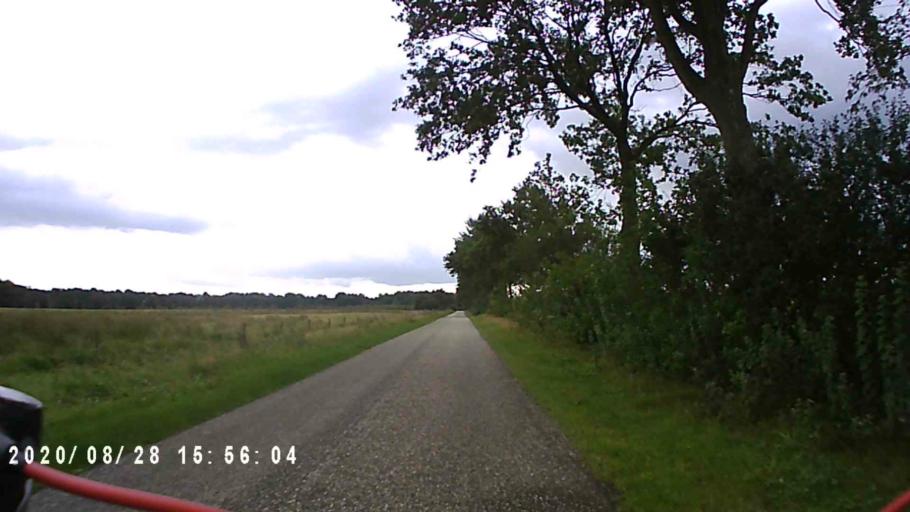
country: NL
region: Drenthe
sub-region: Gemeente Tynaarlo
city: Vries
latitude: 53.1075
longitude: 6.5125
